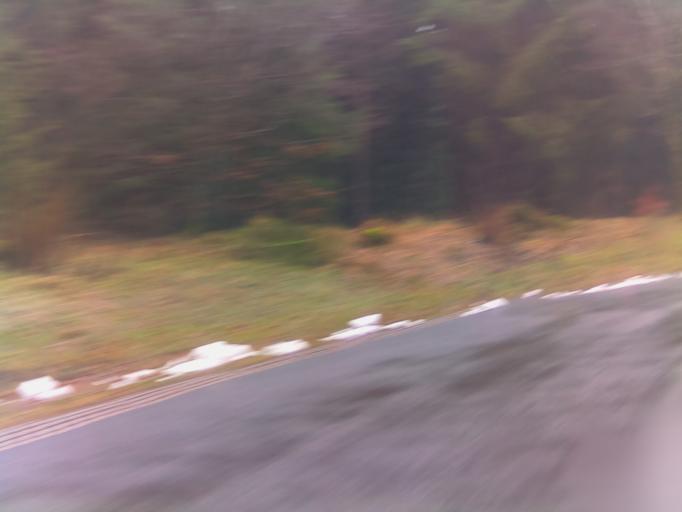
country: DE
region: Thuringia
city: Masserberg
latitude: 50.5305
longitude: 10.9510
